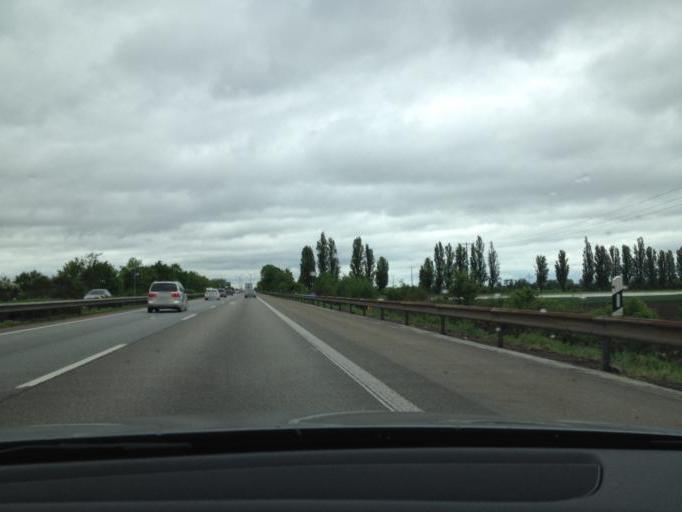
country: DE
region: Rheinland-Pfalz
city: Maxdorf
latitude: 49.4950
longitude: 8.3119
